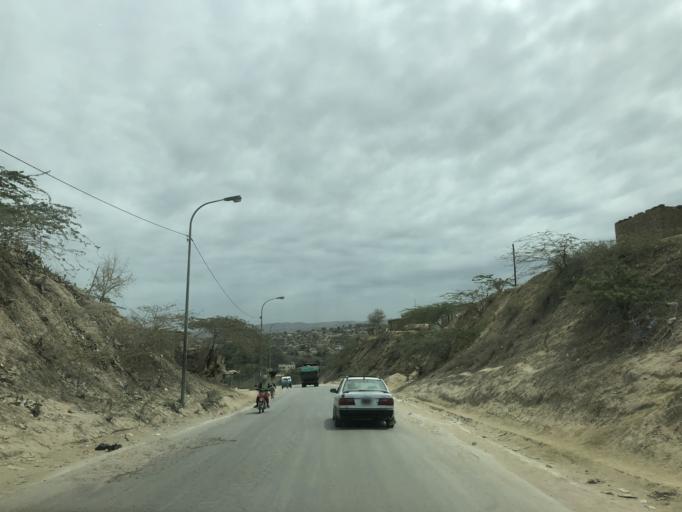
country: AO
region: Cuanza Sul
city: Sumbe
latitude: -11.2233
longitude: 13.8466
